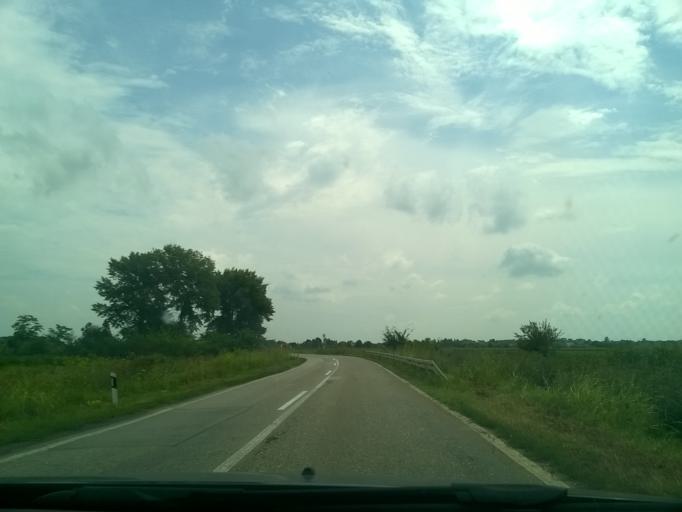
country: RS
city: Hajducica
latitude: 45.2609
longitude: 20.9574
